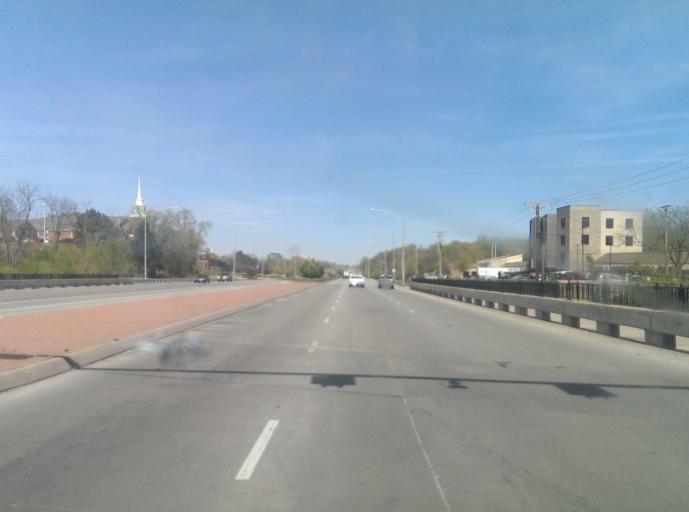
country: US
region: Kansas
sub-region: Johnson County
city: Overland Park
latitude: 38.9419
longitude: -94.6674
